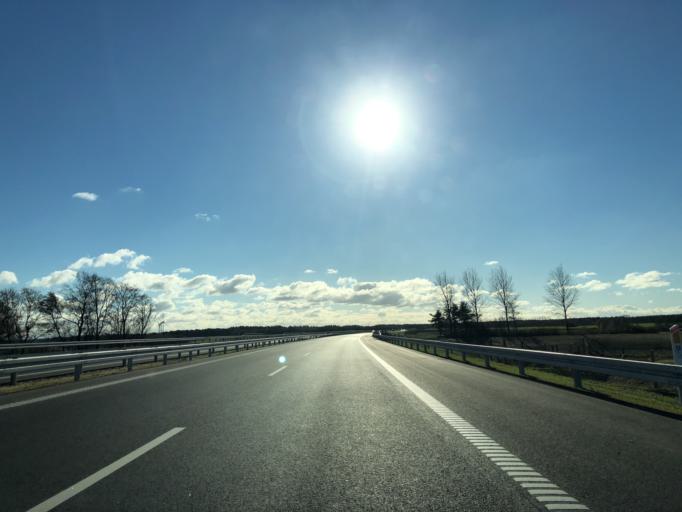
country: DK
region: Central Jutland
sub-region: Herning Kommune
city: Avlum
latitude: 56.3520
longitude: 8.7364
